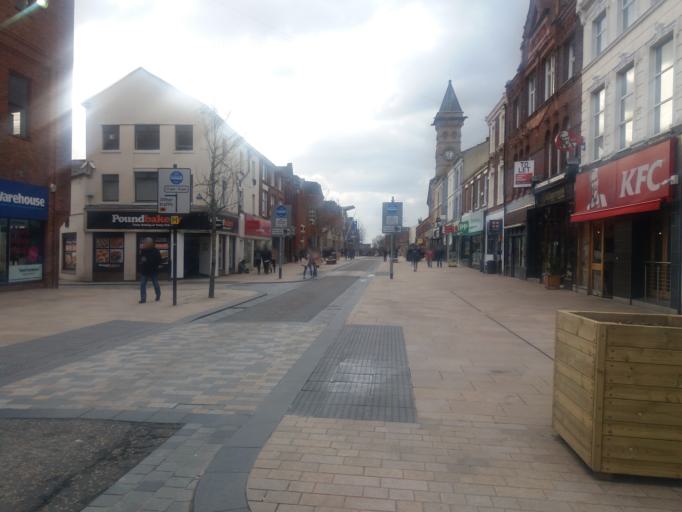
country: GB
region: England
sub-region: Lancashire
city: Preston
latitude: 53.7577
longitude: -2.7034
